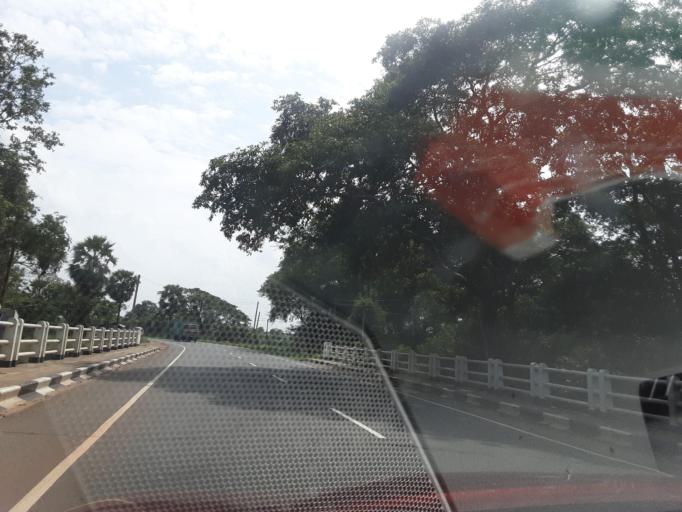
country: LK
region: North Central
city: Anuradhapura
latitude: 8.5109
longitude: 80.5059
